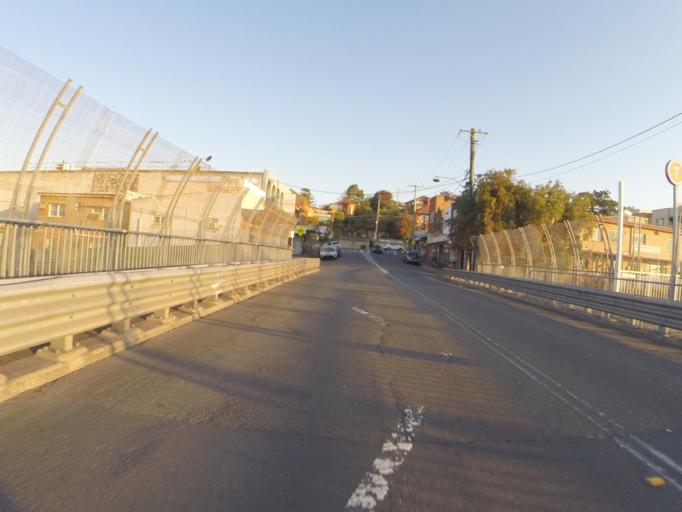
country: AU
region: New South Wales
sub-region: Rockdale
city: Bardwell Valley
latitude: -33.9312
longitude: 151.1254
